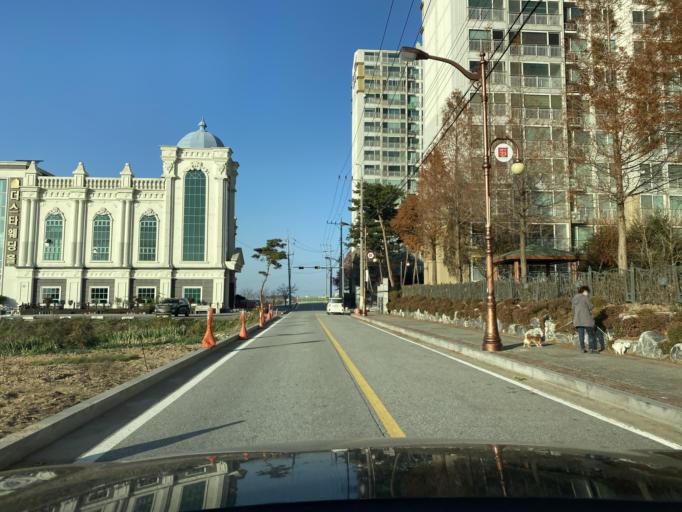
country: KR
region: Chungcheongnam-do
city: Yesan
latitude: 36.6956
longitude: 126.8313
